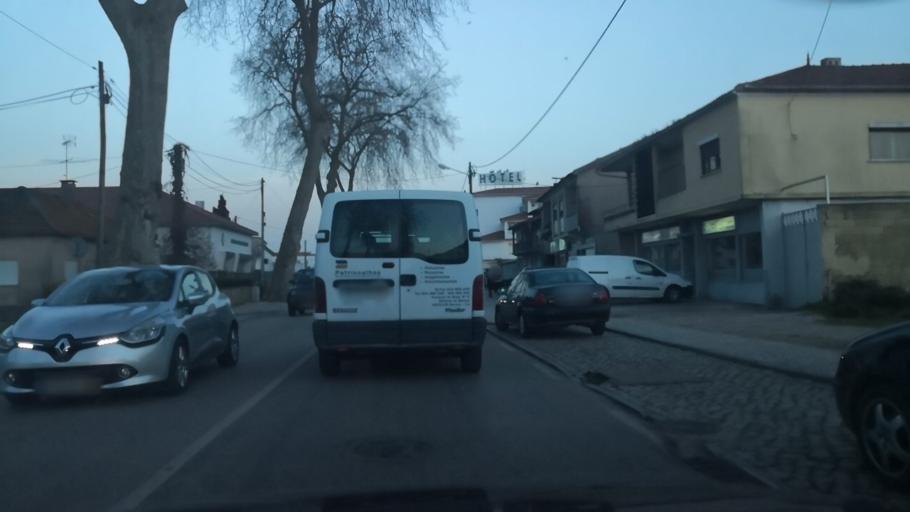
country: PT
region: Leiria
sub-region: Marinha Grande
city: Marinha Grande
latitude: 39.7484
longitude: -8.9155
